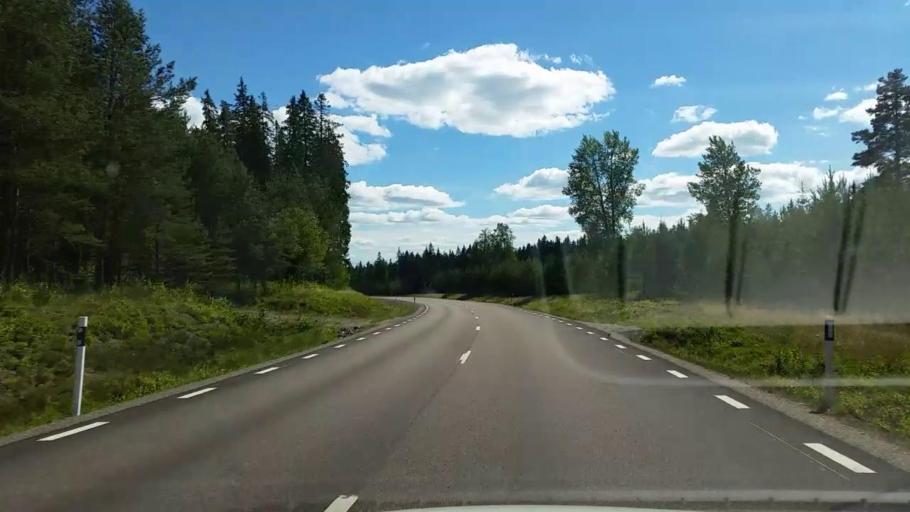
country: SE
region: Dalarna
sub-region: Faluns Kommun
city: Svardsjo
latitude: 60.7627
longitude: 15.7538
